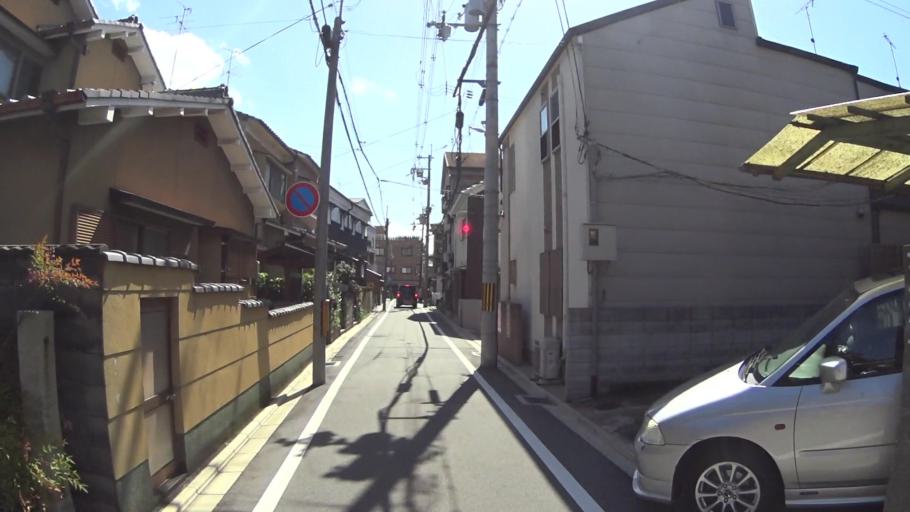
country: JP
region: Kyoto
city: Muko
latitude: 34.9457
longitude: 135.7611
